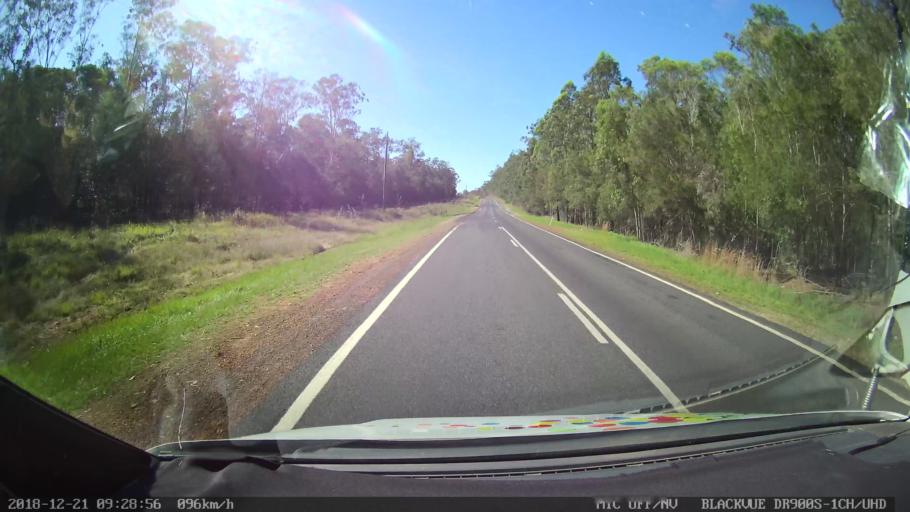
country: AU
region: New South Wales
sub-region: Clarence Valley
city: Maclean
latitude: -29.4244
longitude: 152.9886
